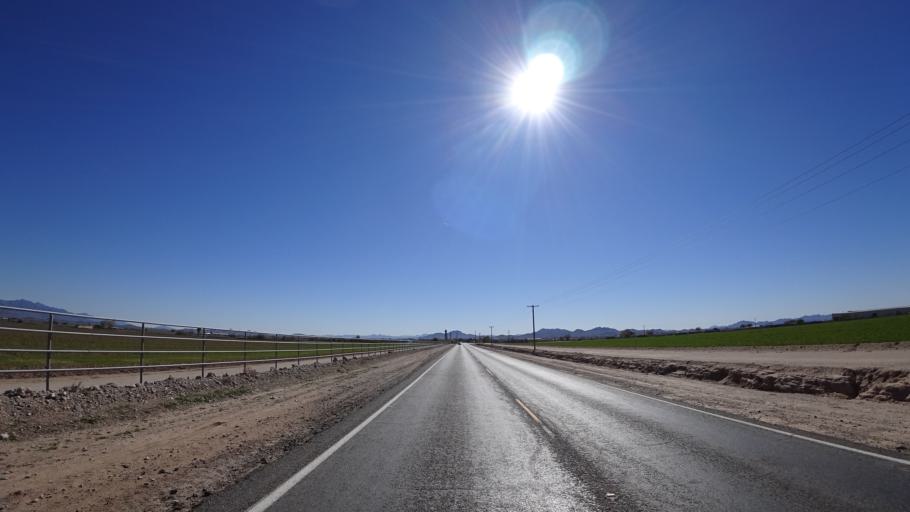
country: US
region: Arizona
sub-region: Maricopa County
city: Buckeye
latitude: 33.3947
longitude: -112.5214
